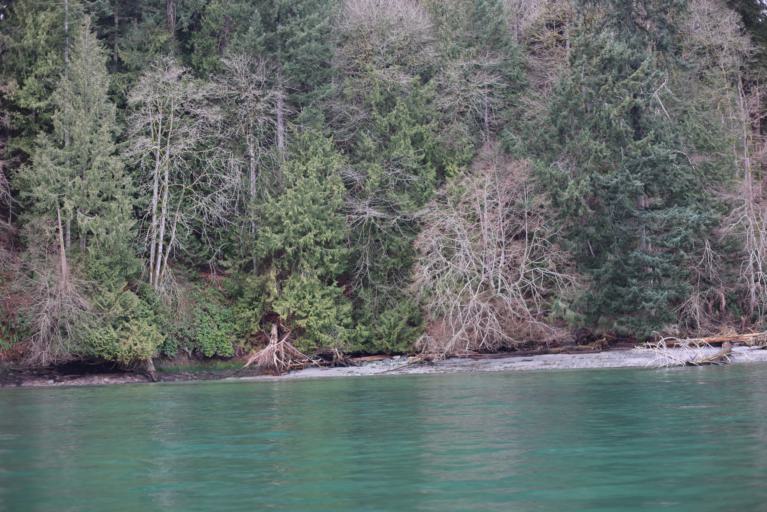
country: CA
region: British Columbia
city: North Saanich
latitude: 48.6836
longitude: -123.5326
